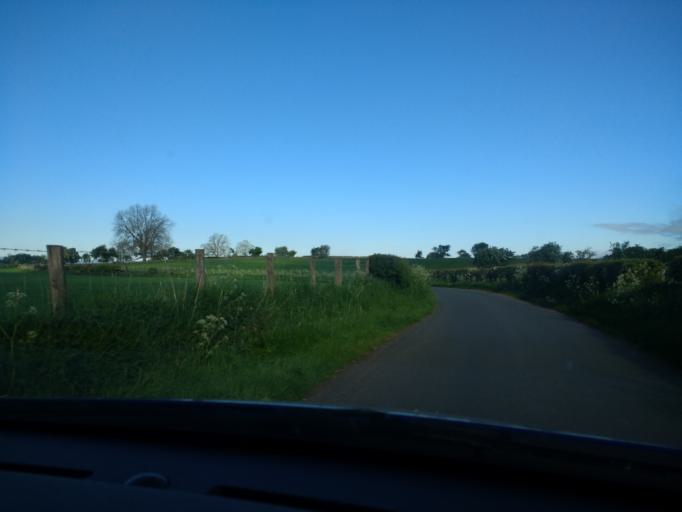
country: GB
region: England
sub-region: Cumbria
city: Appleby-in-Westmorland
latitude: 54.6744
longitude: -2.5748
